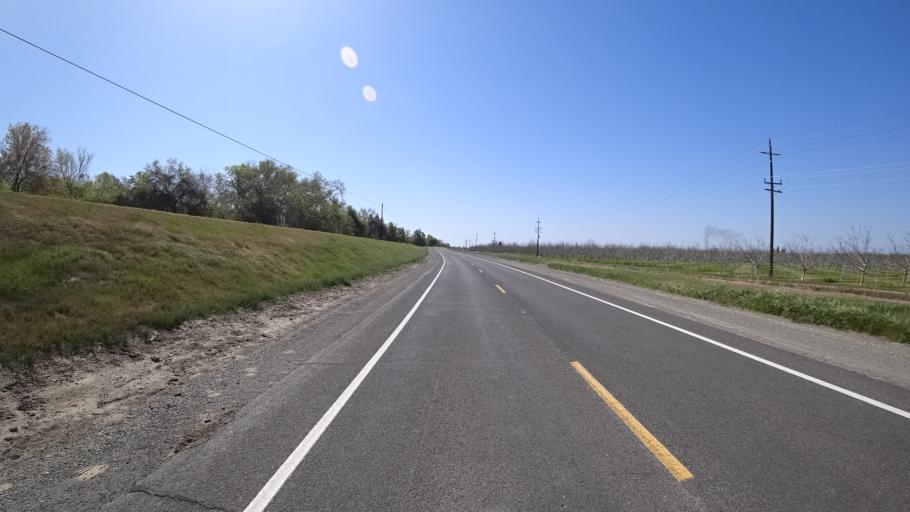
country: US
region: California
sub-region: Glenn County
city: Willows
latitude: 39.4334
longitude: -122.0110
